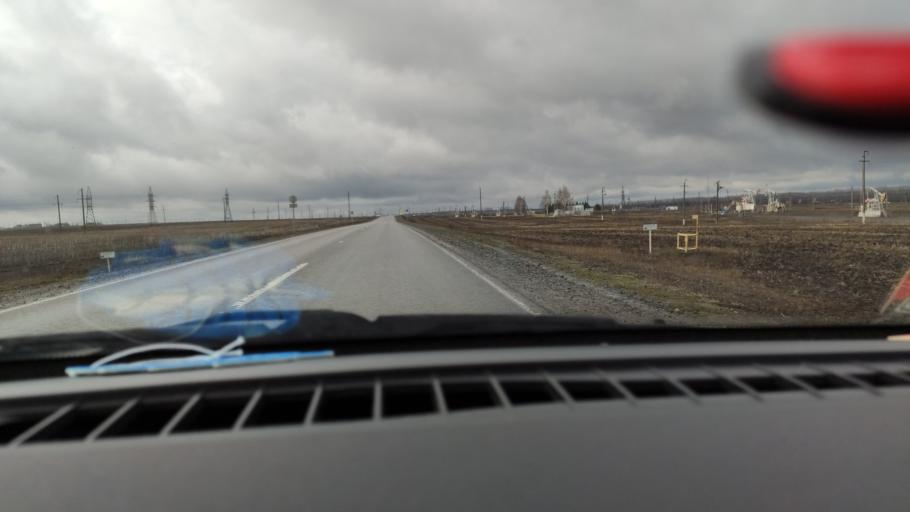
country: RU
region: Tatarstan
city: Nurlat
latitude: 54.4794
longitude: 50.8434
